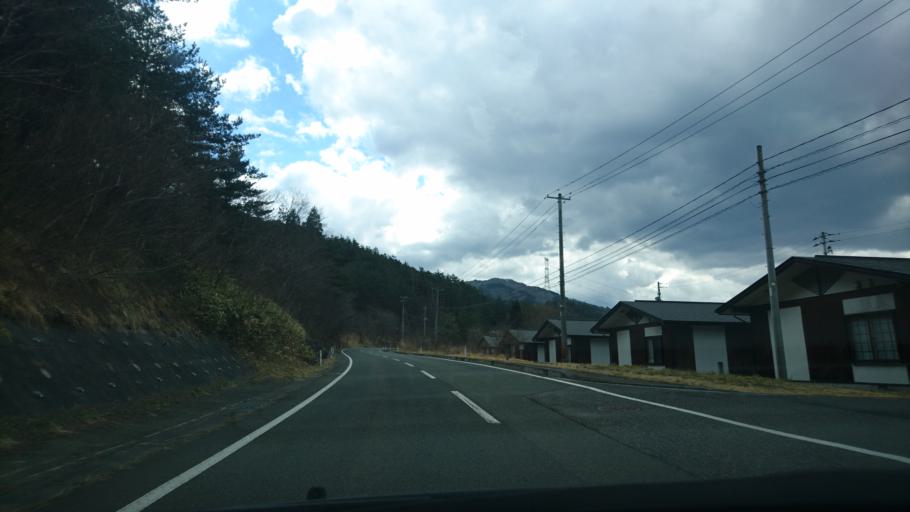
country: JP
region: Iwate
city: Tono
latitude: 39.3506
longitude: 141.3432
